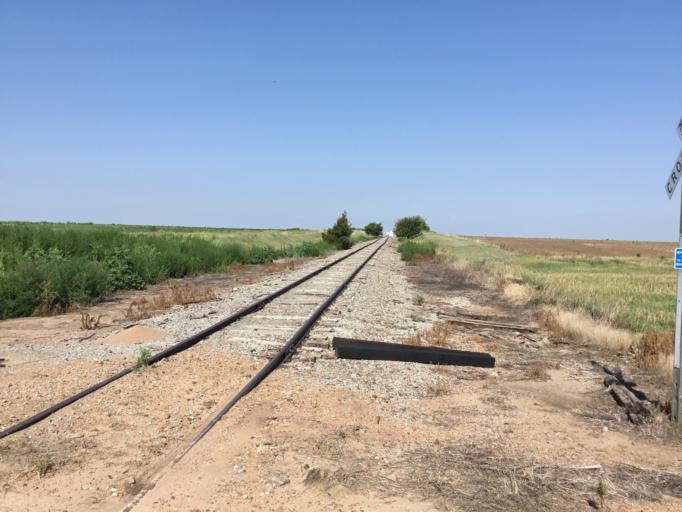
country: US
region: Kansas
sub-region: Pratt County
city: Pratt
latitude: 37.5101
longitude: -98.7931
